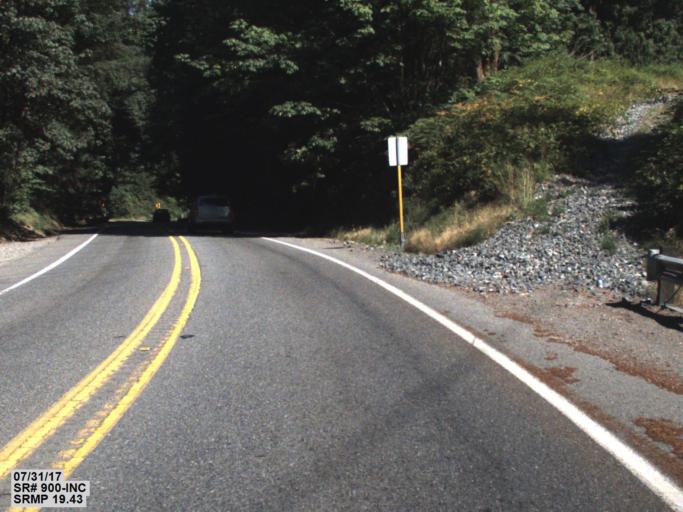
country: US
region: Washington
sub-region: King County
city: Issaquah
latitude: 47.5192
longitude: -122.0695
